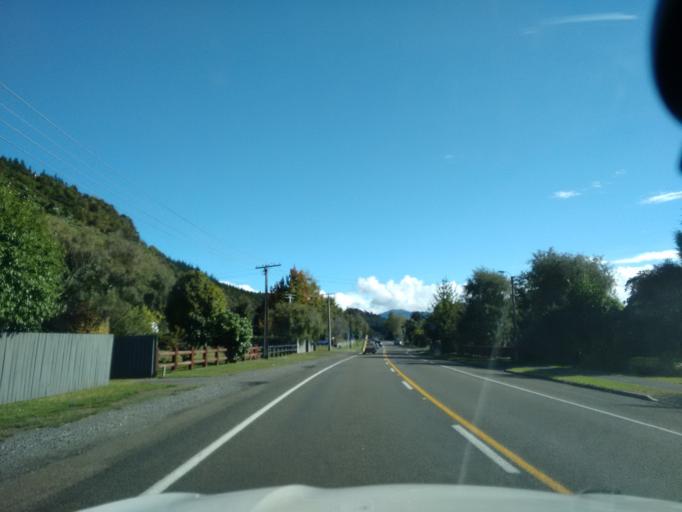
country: NZ
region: Waikato
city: Turangi
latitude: -38.9331
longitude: 175.8746
